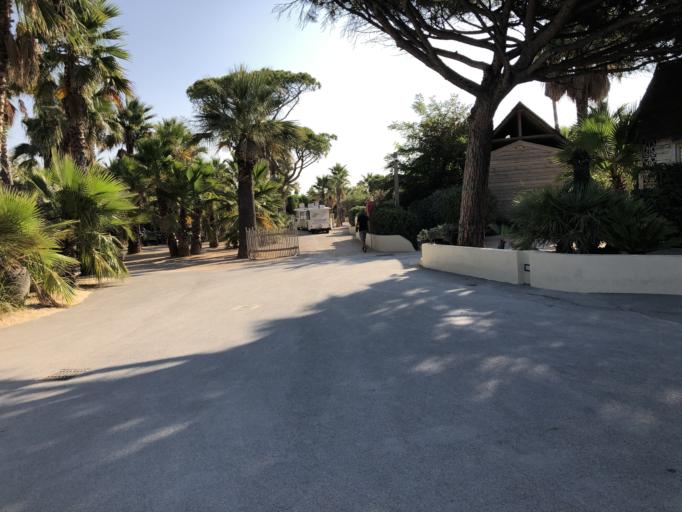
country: FR
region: Provence-Alpes-Cote d'Azur
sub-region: Departement du Var
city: Gassin
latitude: 43.2767
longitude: 6.5815
